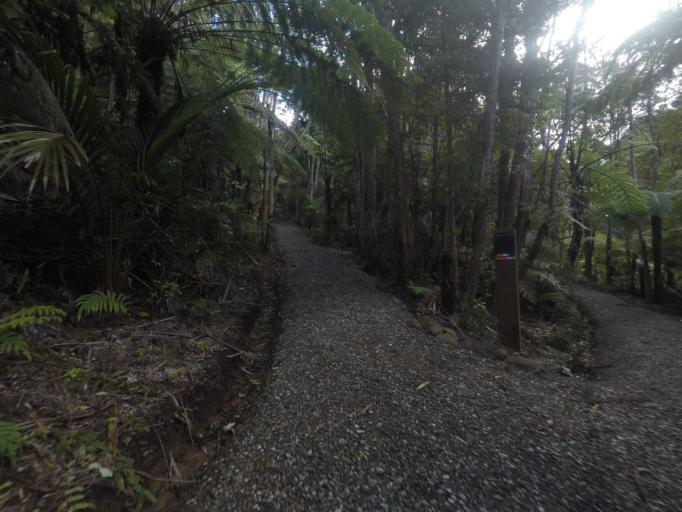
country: NZ
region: Auckland
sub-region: Auckland
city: Titirangi
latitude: -37.0020
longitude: 174.5562
